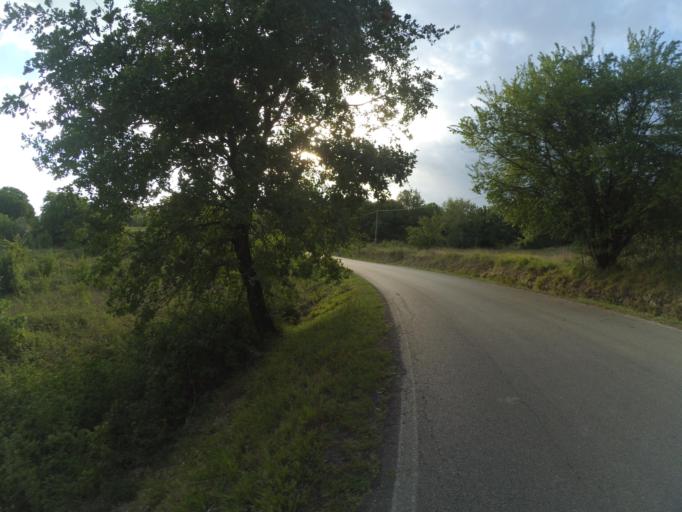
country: IT
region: Tuscany
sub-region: Province of Arezzo
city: Castiglion Fibocchi
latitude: 43.5308
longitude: 11.7691
